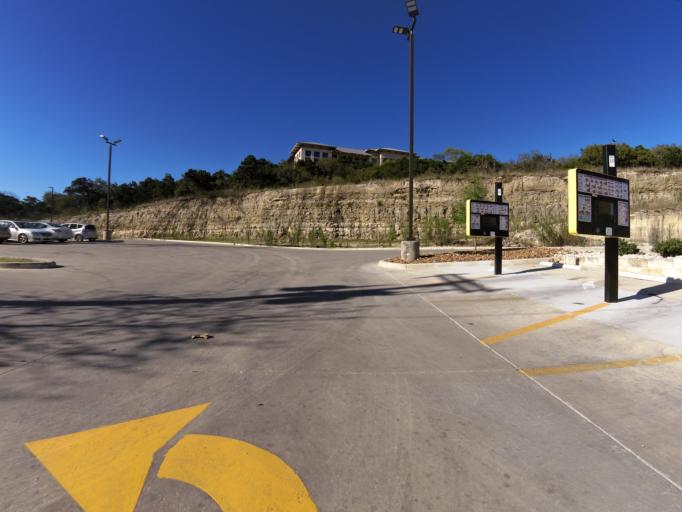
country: US
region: Texas
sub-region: Bexar County
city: Shavano Park
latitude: 29.6166
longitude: -98.6049
